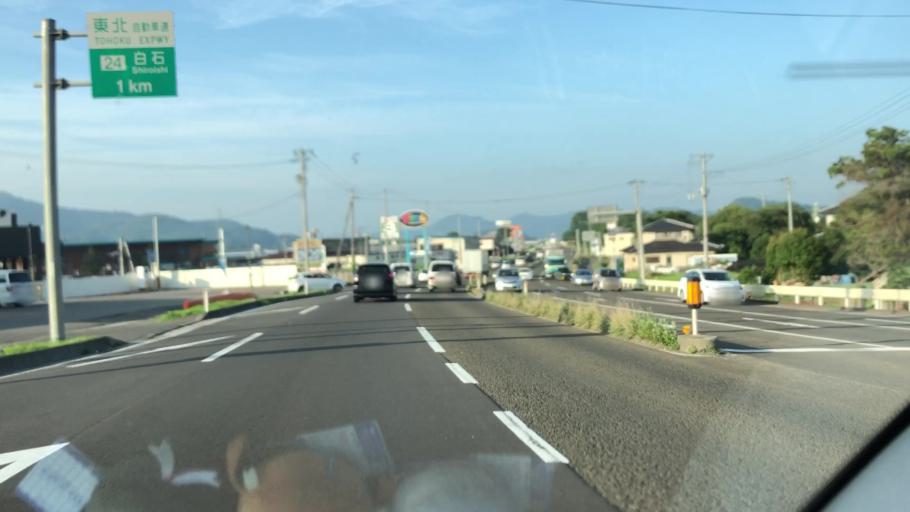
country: JP
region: Miyagi
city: Shiroishi
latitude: 38.0293
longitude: 140.6302
